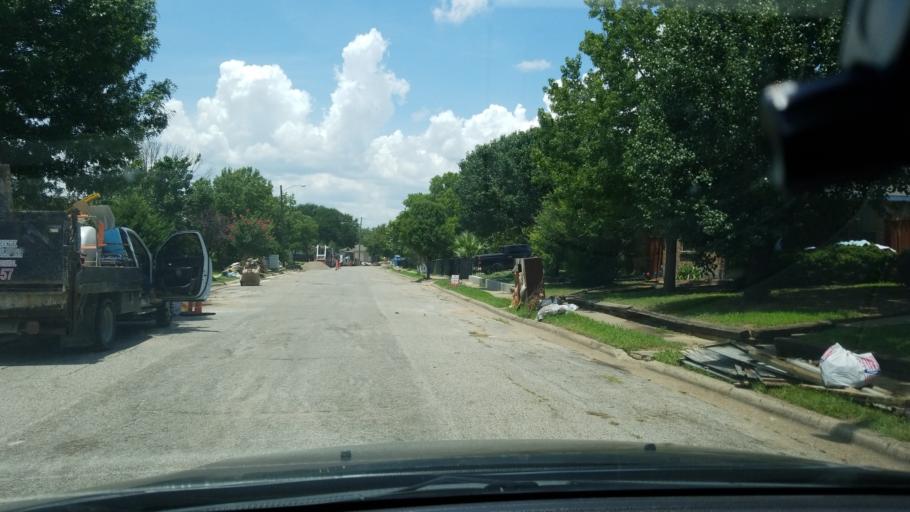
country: US
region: Texas
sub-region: Dallas County
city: Balch Springs
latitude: 32.7435
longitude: -96.6461
